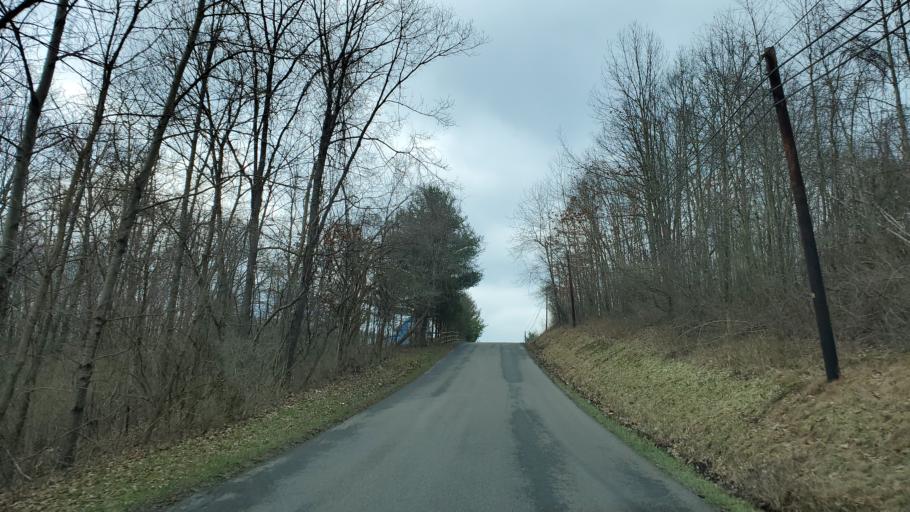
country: US
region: Ohio
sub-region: Licking County
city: Newark
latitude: 40.0387
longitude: -82.3710
